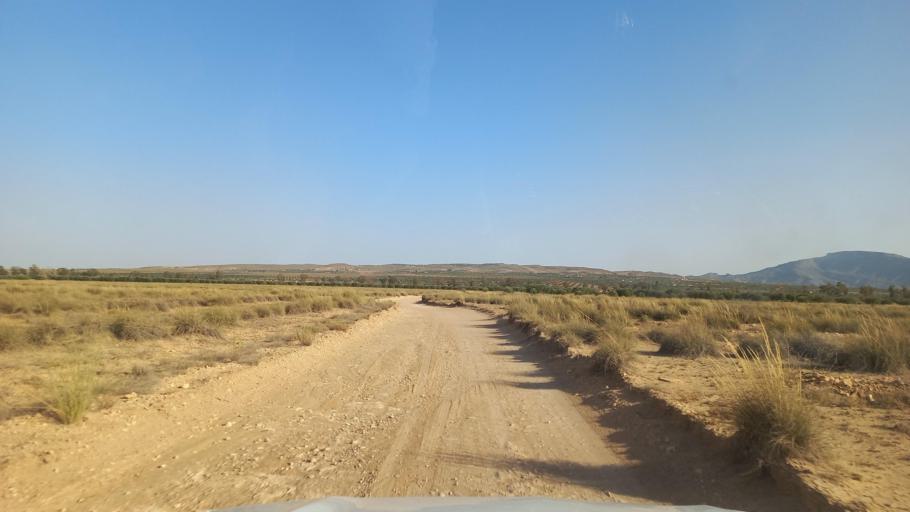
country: TN
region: Al Qasrayn
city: Kasserine
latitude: 35.2308
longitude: 8.9405
